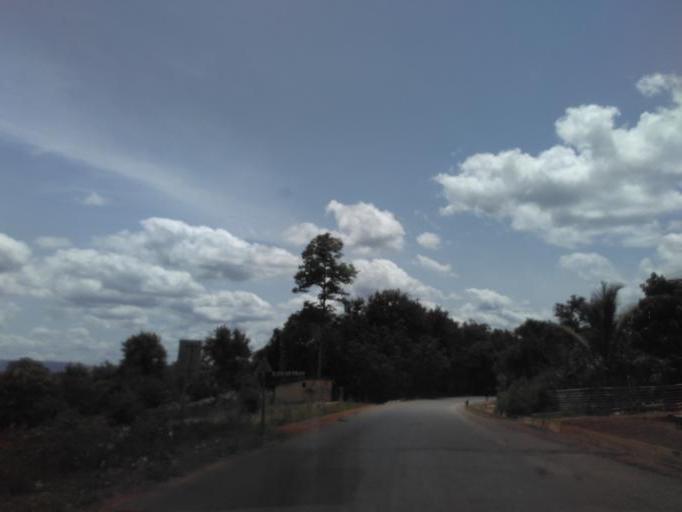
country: GH
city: Akropong
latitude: 6.0856
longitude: -0.1004
